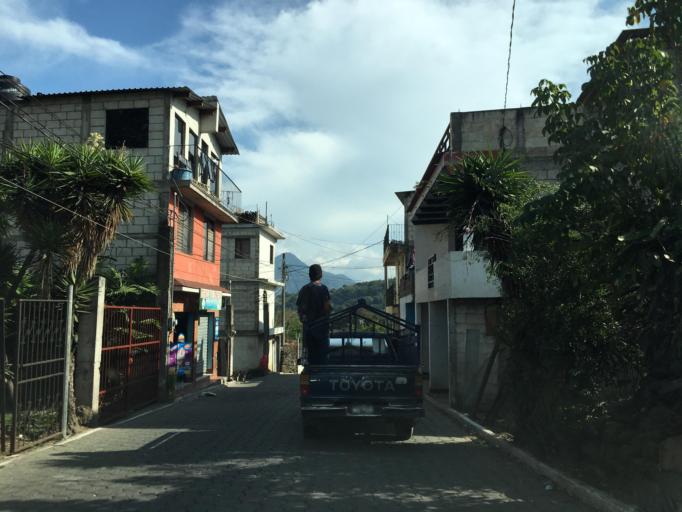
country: GT
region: Solola
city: San Antonio Palopo
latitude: 14.6659
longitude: -91.1646
